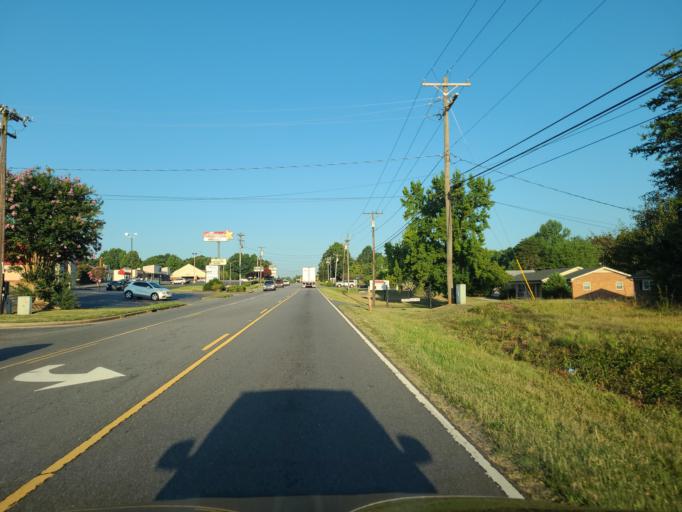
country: US
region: North Carolina
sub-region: Catawba County
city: Mountain View
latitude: 35.6865
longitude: -81.3686
